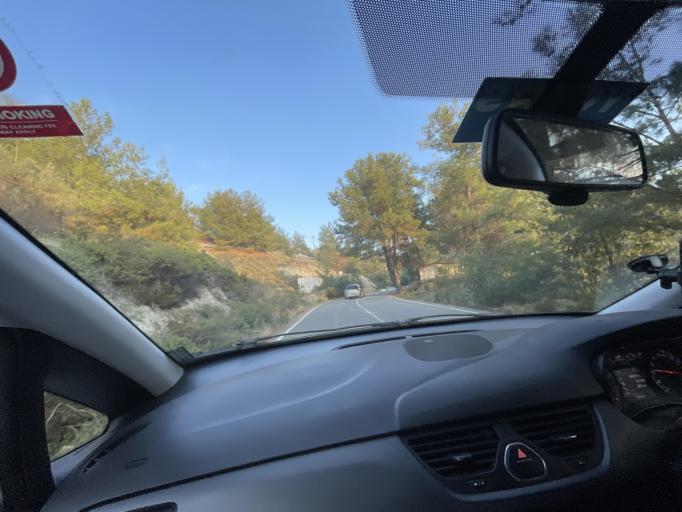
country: CY
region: Limassol
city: Pelendri
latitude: 34.8927
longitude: 32.9679
